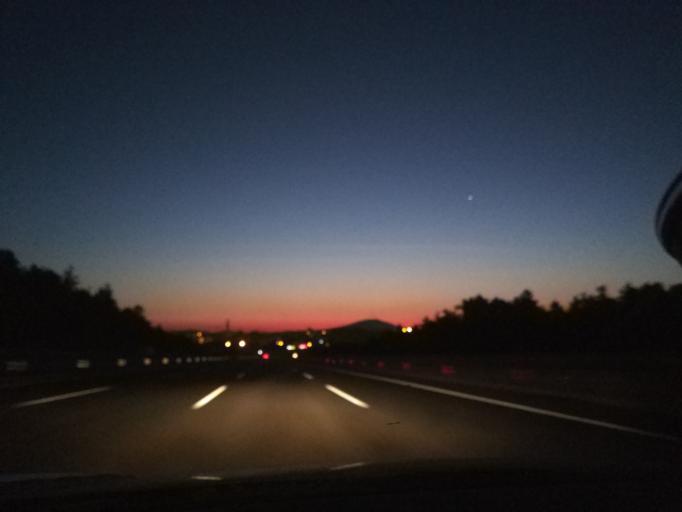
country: TR
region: Istanbul
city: Sancaktepe
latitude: 41.0448
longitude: 29.2267
